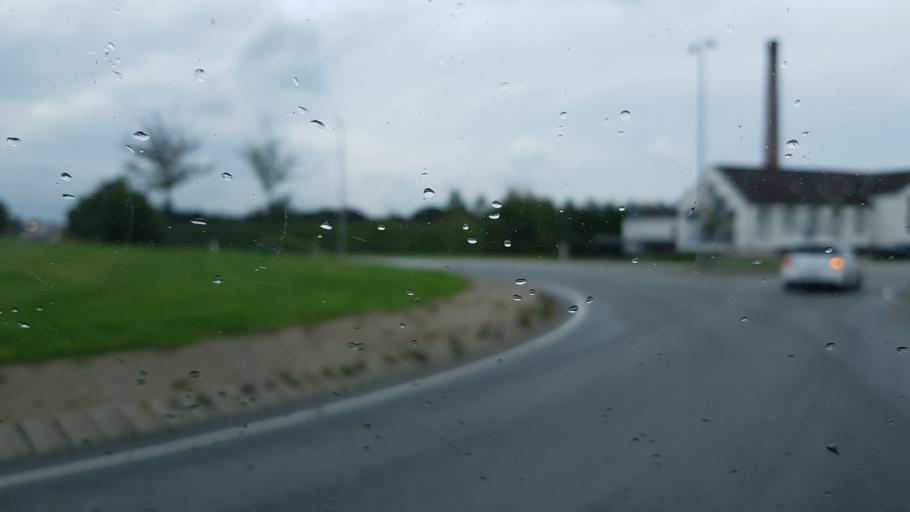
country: DK
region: Central Jutland
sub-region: Horsens Kommune
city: Horsens
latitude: 55.8972
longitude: 9.7524
